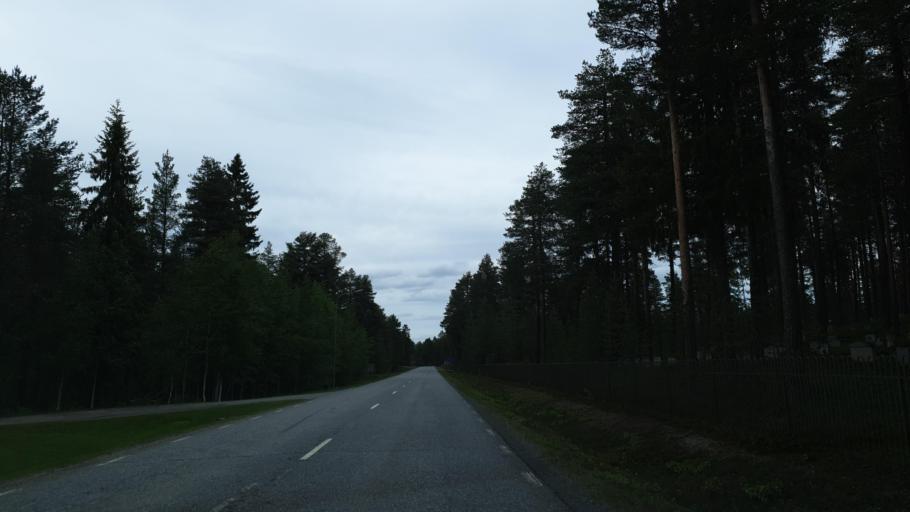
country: SE
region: Vaesterbotten
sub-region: Sorsele Kommun
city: Sorsele
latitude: 65.5464
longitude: 17.5082
